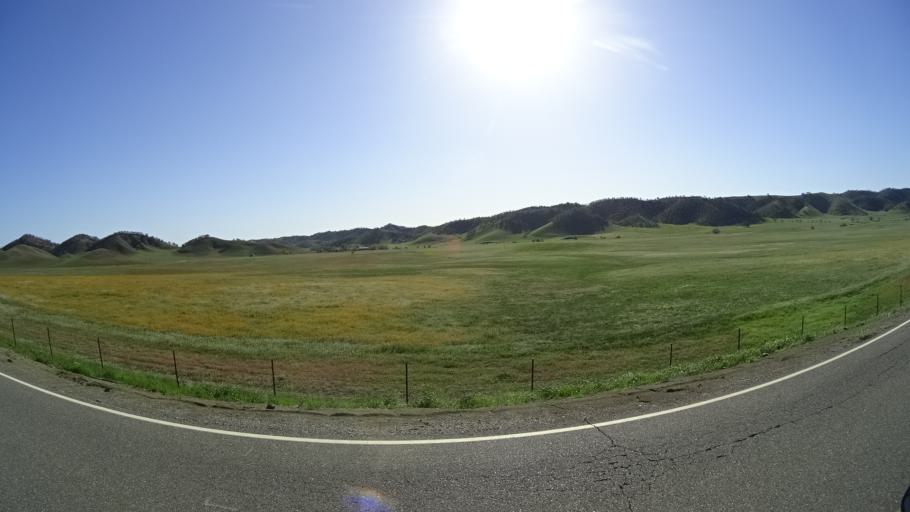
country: US
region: California
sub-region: Tehama County
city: Rancho Tehama Reserve
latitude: 39.7583
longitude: -122.5253
